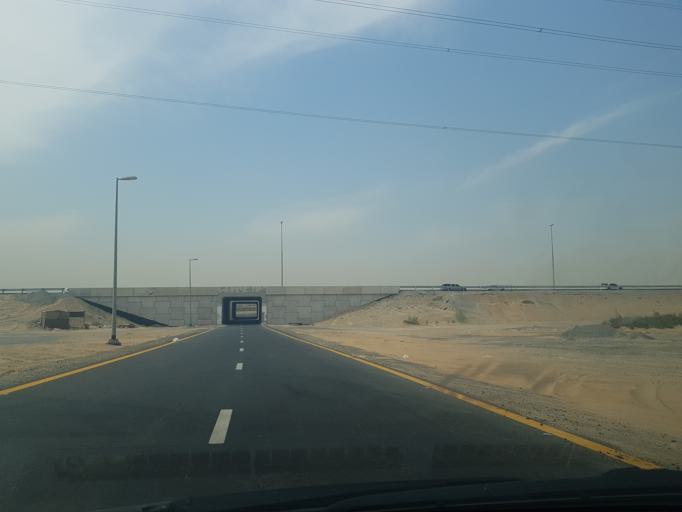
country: AE
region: Ash Shariqah
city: Sharjah
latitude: 25.2866
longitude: 55.5900
